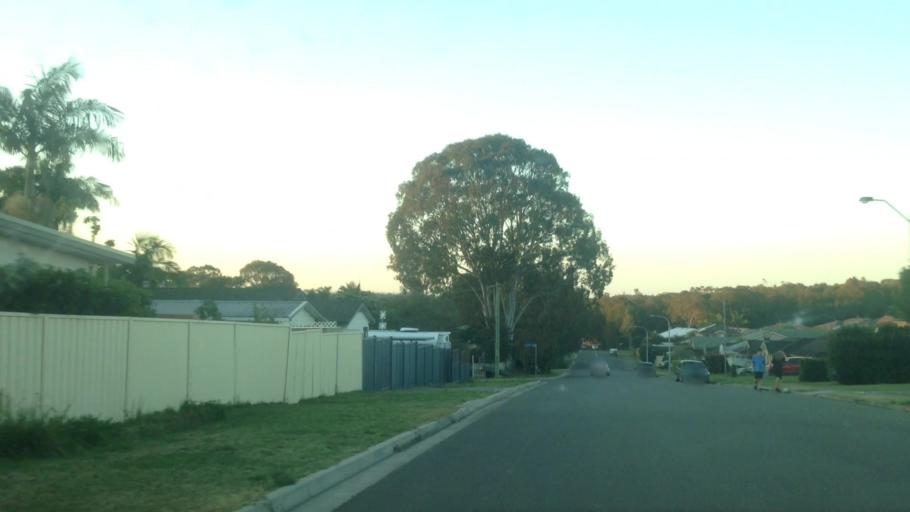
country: AU
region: New South Wales
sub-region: Wyong Shire
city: Kingfisher Shores
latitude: -33.1450
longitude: 151.5203
